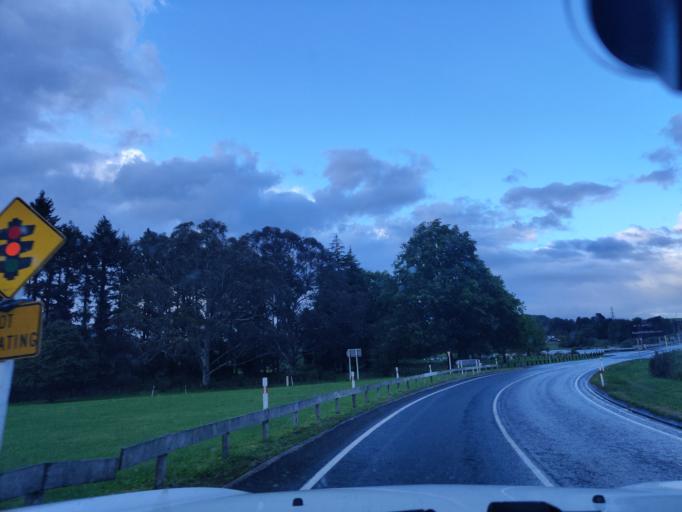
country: NZ
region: Waikato
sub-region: South Waikato District
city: Tokoroa
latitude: -38.4183
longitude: 175.8111
